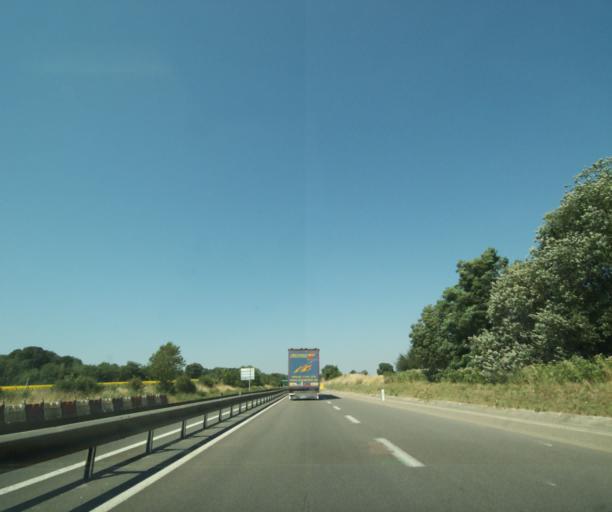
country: FR
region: Champagne-Ardenne
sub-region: Departement de la Haute-Marne
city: Saint-Dizier
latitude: 48.6214
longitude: 4.9583
